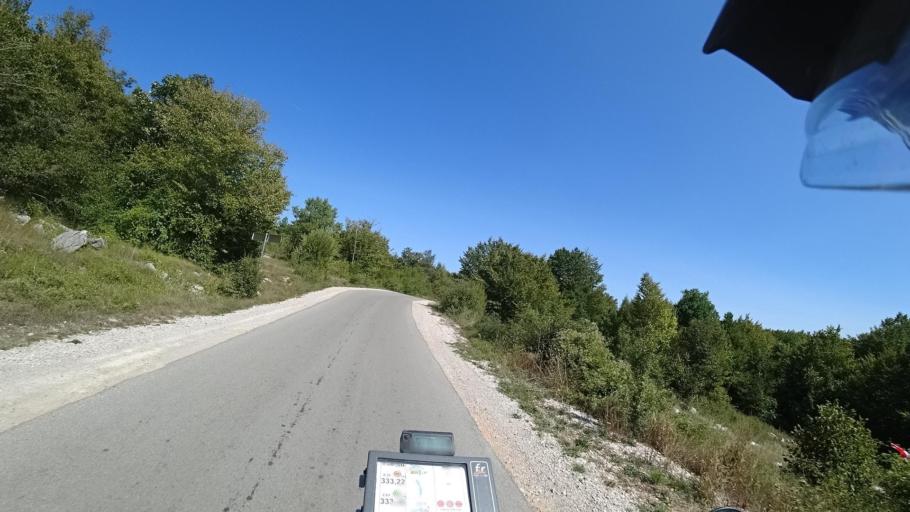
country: HR
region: Licko-Senjska
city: Popovaca
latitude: 44.7304
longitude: 15.3015
